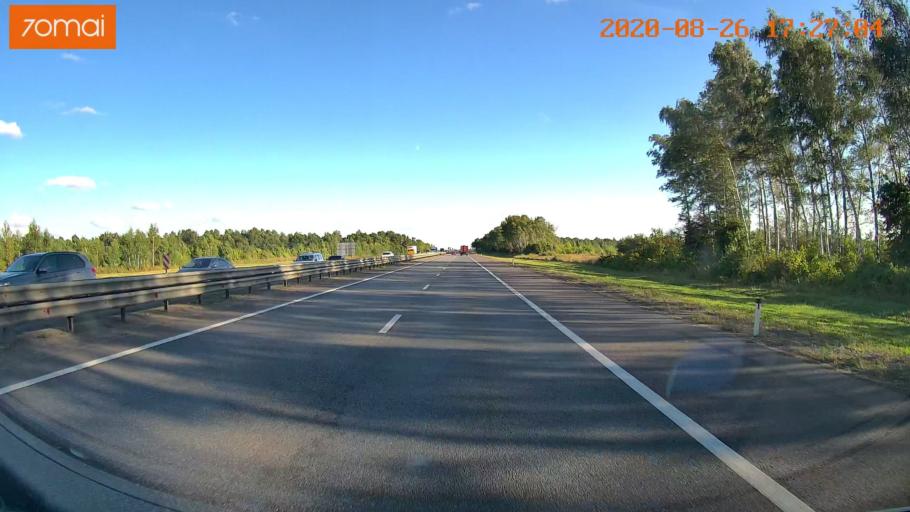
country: RU
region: Tula
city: Kazachka
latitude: 53.4779
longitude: 38.1219
